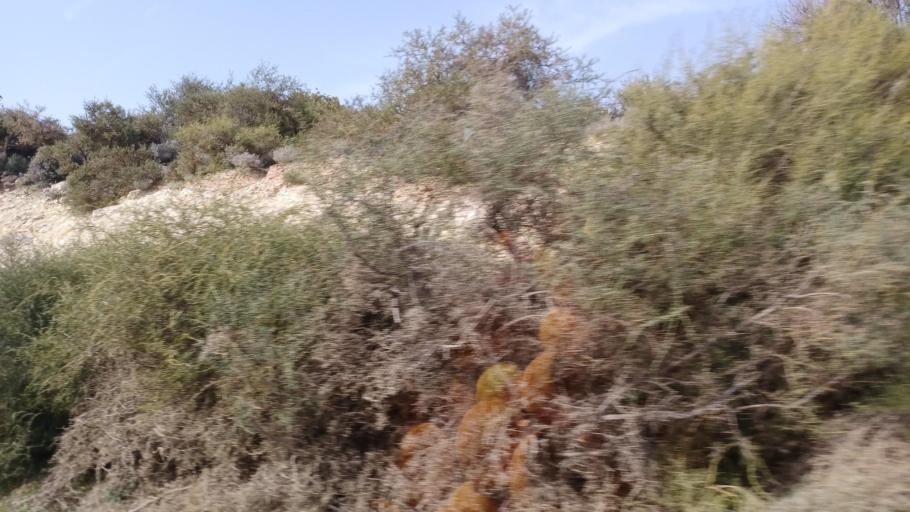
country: CY
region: Limassol
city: Pissouri
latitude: 34.7616
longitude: 32.6971
